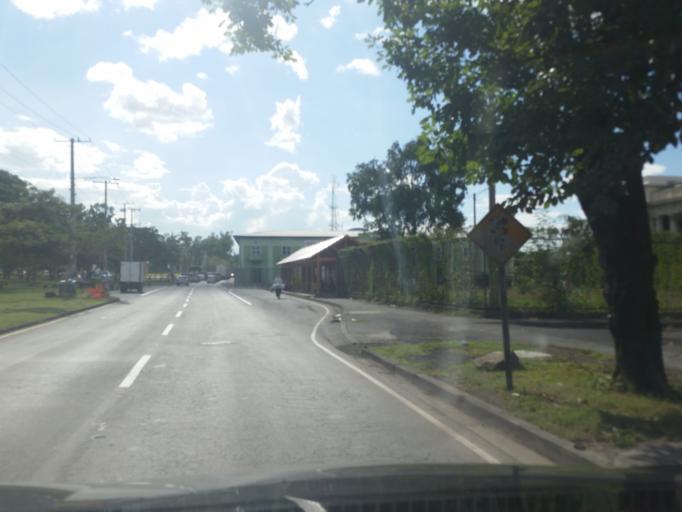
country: NI
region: Managua
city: Managua
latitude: 12.1548
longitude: -86.2714
